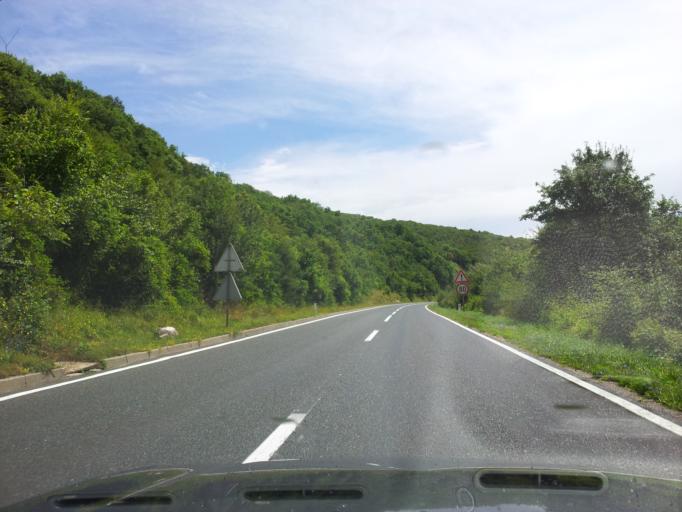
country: BA
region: Federation of Bosnia and Herzegovina
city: Bihac
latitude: 44.6152
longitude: 15.7393
